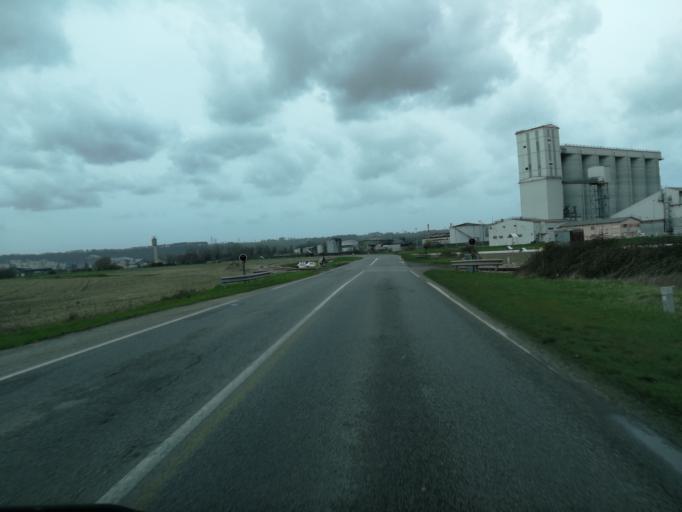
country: FR
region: Haute-Normandie
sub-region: Departement de l'Eure
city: Quillebeuf-sur-Seine
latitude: 49.4859
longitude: 0.5185
